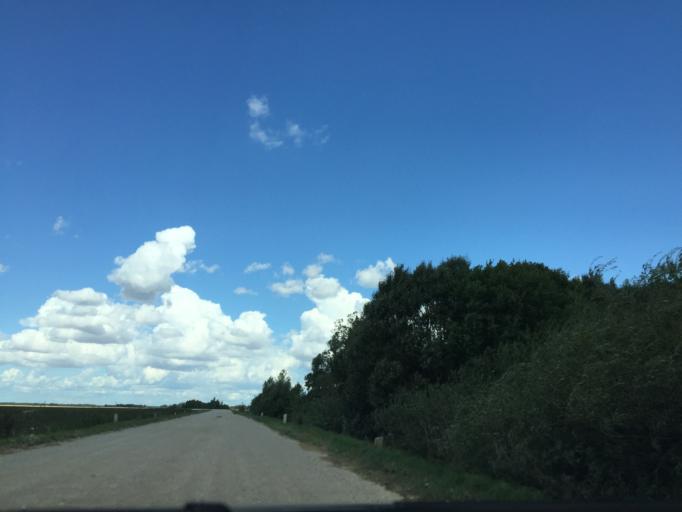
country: LV
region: Rundales
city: Pilsrundale
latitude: 56.3011
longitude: 23.9873
